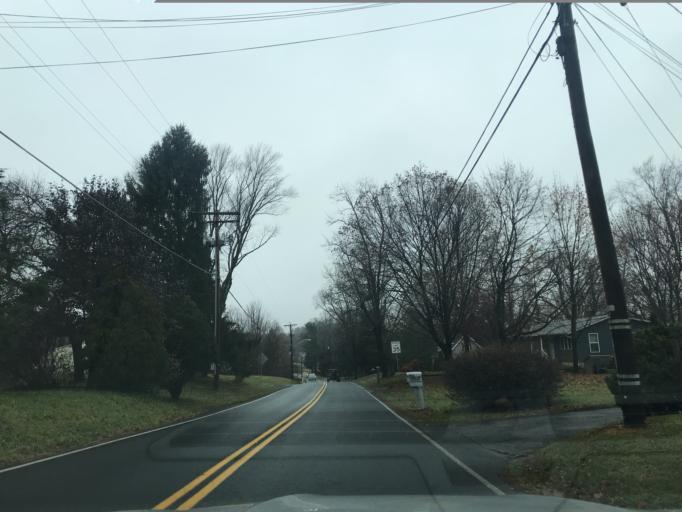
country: US
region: Maryland
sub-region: Harford County
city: South Bel Air
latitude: 39.5667
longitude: -76.3187
